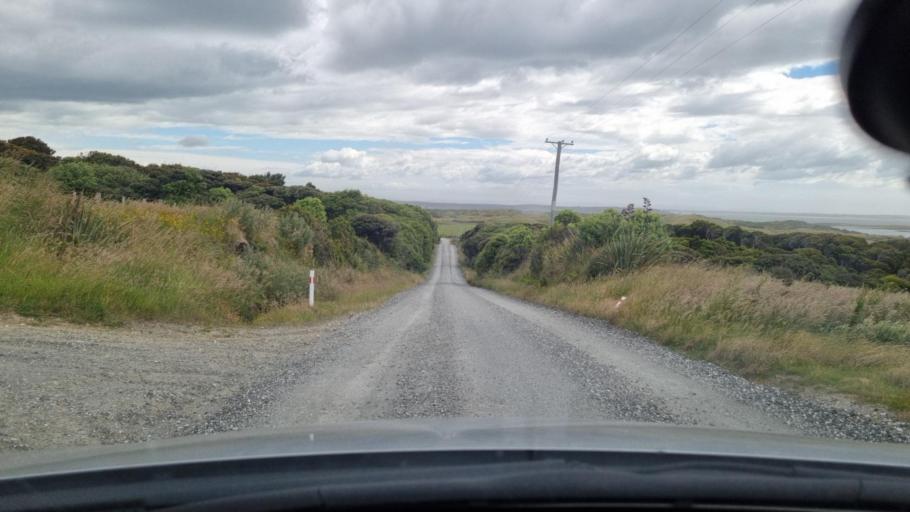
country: NZ
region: Southland
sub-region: Invercargill City
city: Bluff
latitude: -46.5251
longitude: 168.2705
